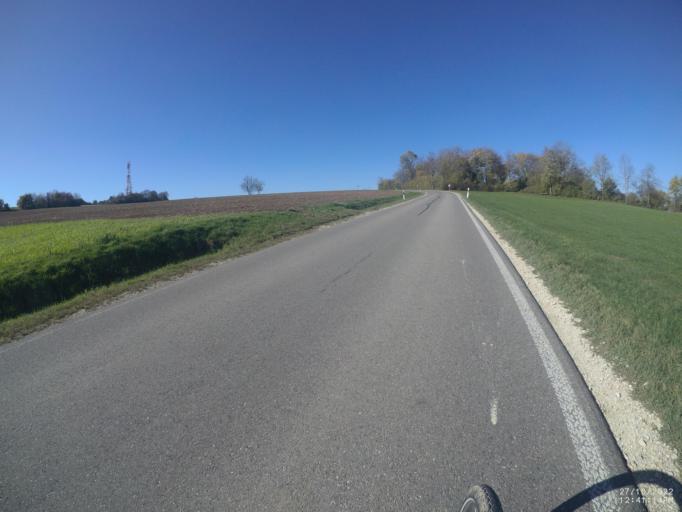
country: DE
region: Baden-Wuerttemberg
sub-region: Regierungsbezirk Stuttgart
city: Hohenstadt
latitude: 48.5526
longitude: 9.6778
